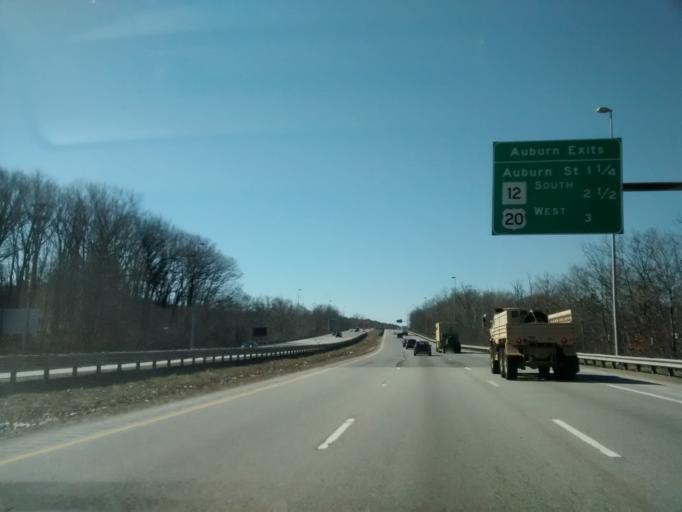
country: US
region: Massachusetts
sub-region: Worcester County
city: Auburn
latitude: 42.2279
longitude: -71.8262
